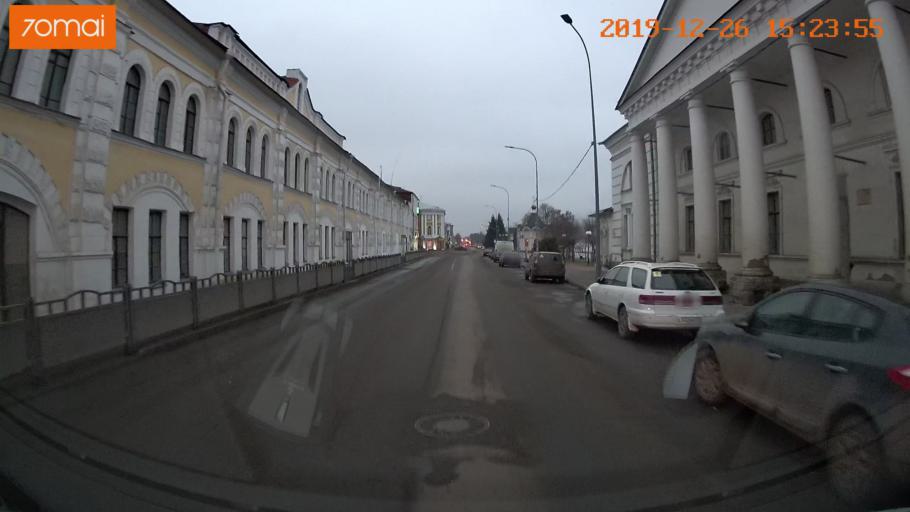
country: RU
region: Jaroslavl
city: Rybinsk
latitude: 58.0496
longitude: 38.8549
